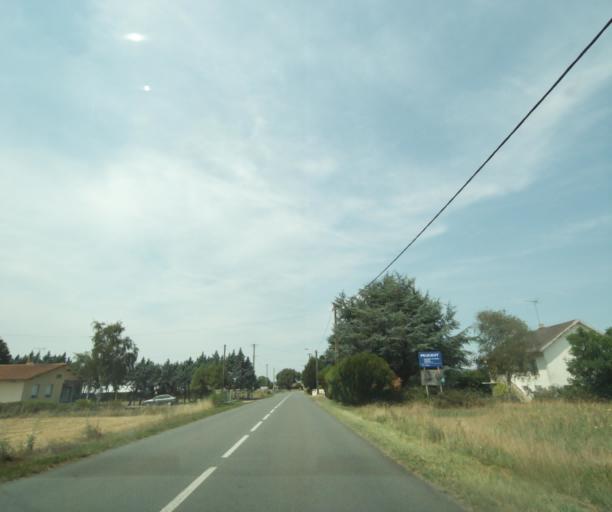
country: FR
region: Poitou-Charentes
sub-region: Departement de la Vienne
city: Chauvigny
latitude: 46.4857
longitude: 0.6533
